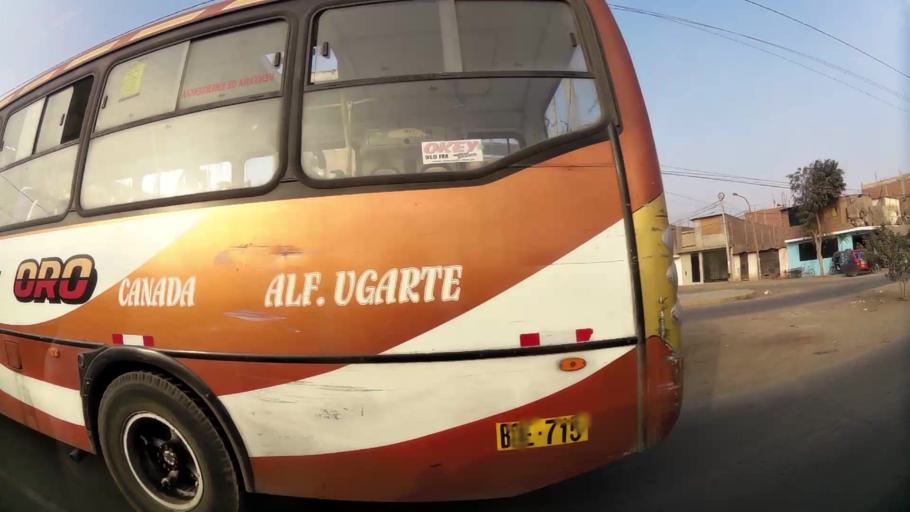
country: PE
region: Lima
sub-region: Lima
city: Independencia
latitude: -11.9529
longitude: -77.0851
